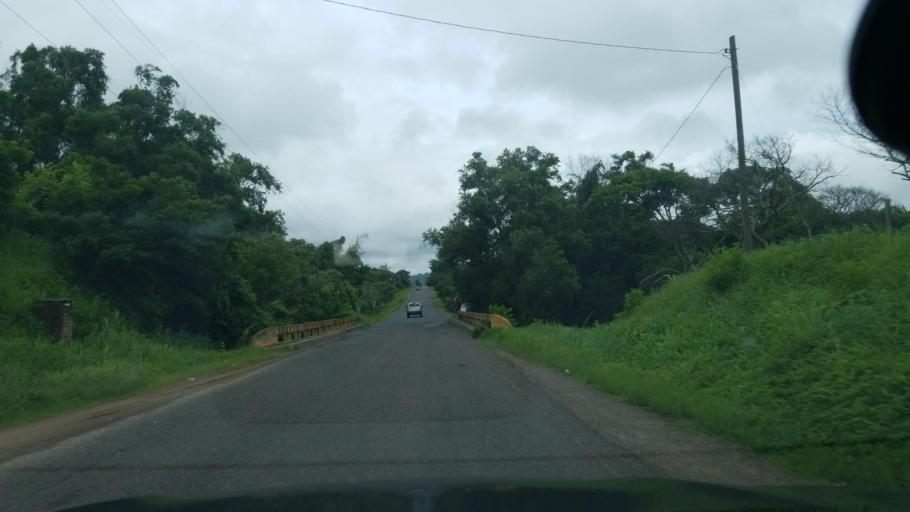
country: HN
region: Choluteca
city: San Marcos de Colon
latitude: 13.4162
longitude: -86.8364
